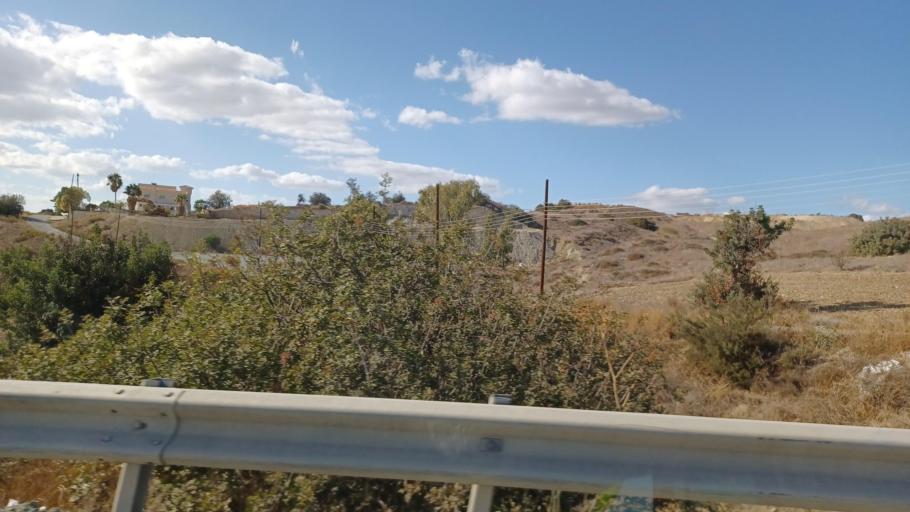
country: CY
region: Limassol
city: Pyrgos
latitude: 34.7429
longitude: 33.2110
